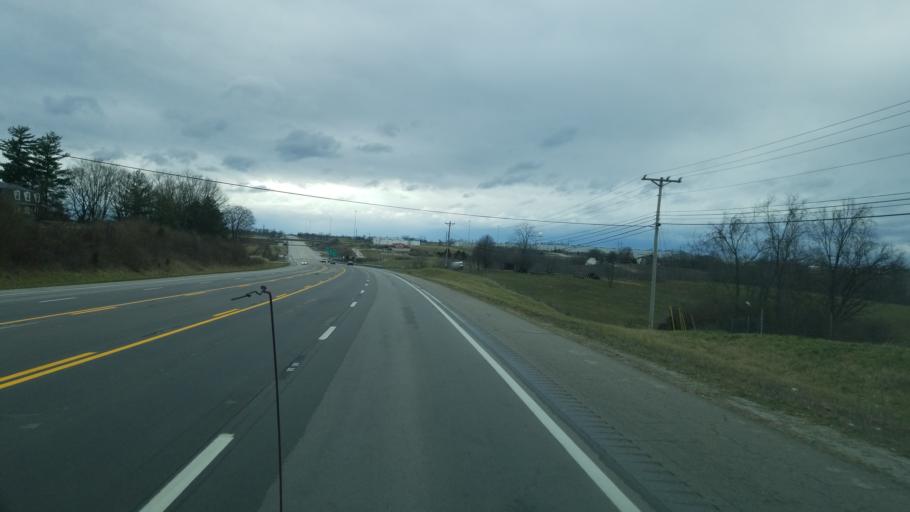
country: US
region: Ohio
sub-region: Brown County
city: Aberdeen
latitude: 38.6416
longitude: -83.8202
